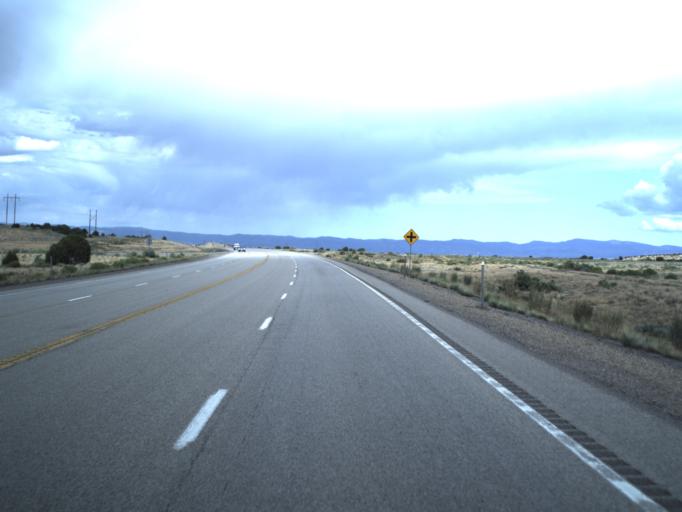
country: US
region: Utah
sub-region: Carbon County
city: Wellington
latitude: 39.5456
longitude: -110.6199
